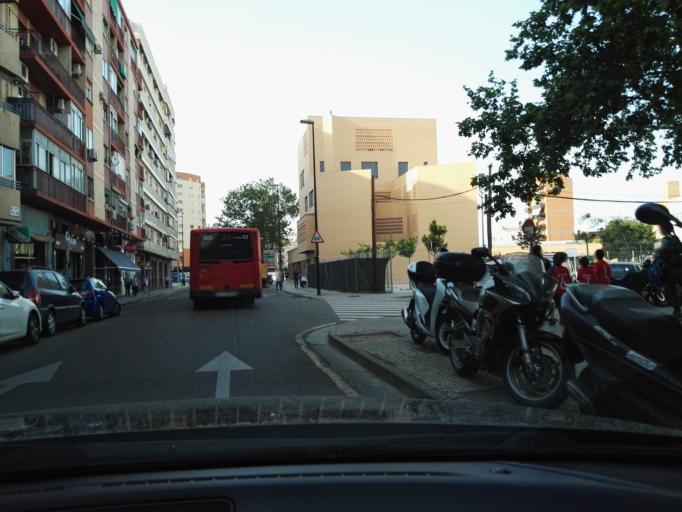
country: ES
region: Aragon
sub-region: Provincia de Zaragoza
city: Zaragoza
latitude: 41.6389
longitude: -0.8740
